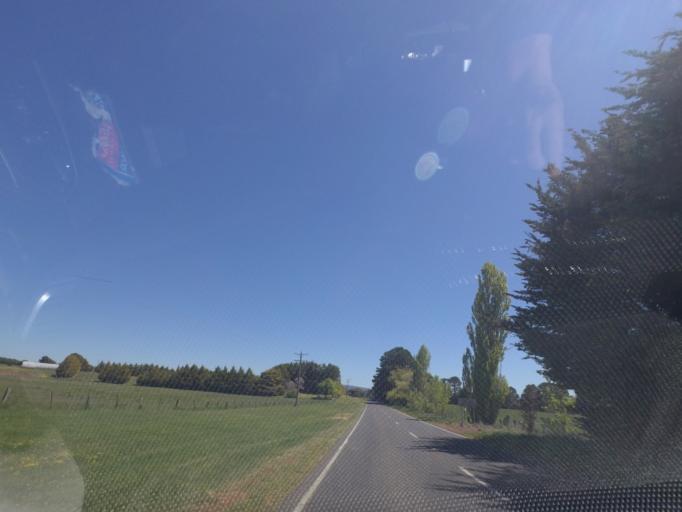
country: AU
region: Victoria
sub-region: Hume
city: Sunbury
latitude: -37.2799
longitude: 144.7487
